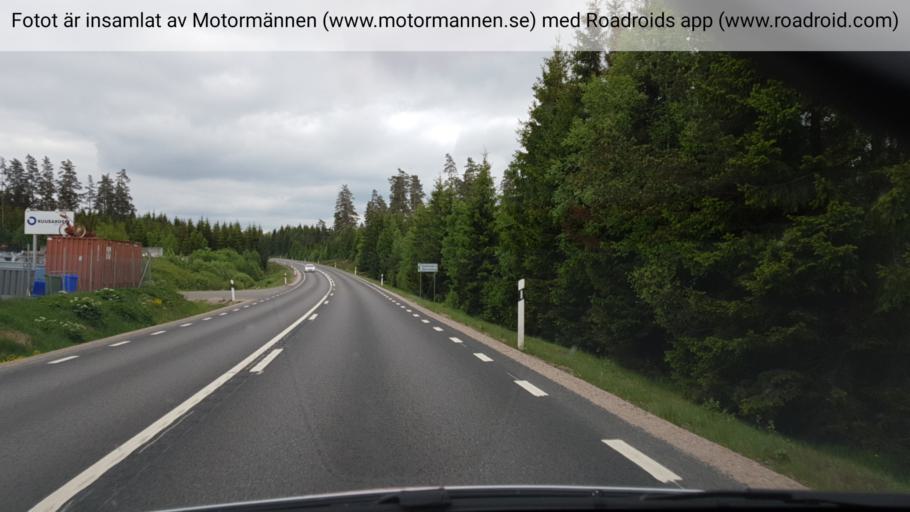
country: SE
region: Joenkoeping
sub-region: Vetlanda Kommun
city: Vetlanda
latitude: 57.2607
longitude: 15.1277
